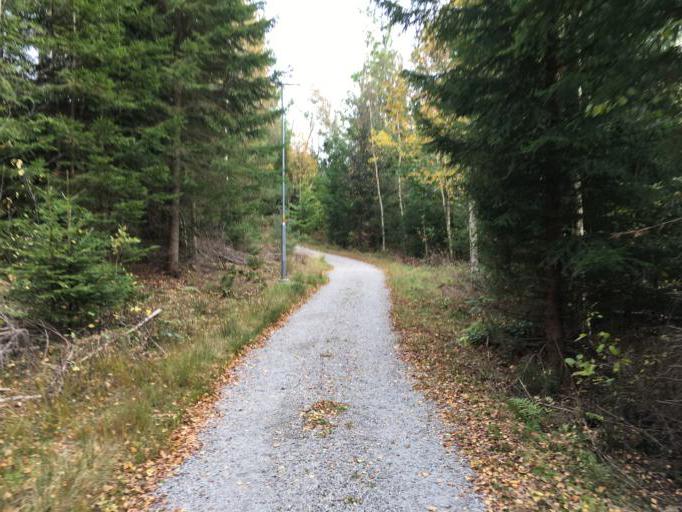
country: SE
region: Skane
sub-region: Hassleholms Kommun
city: Hassleholm
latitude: 56.1556
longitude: 13.7278
